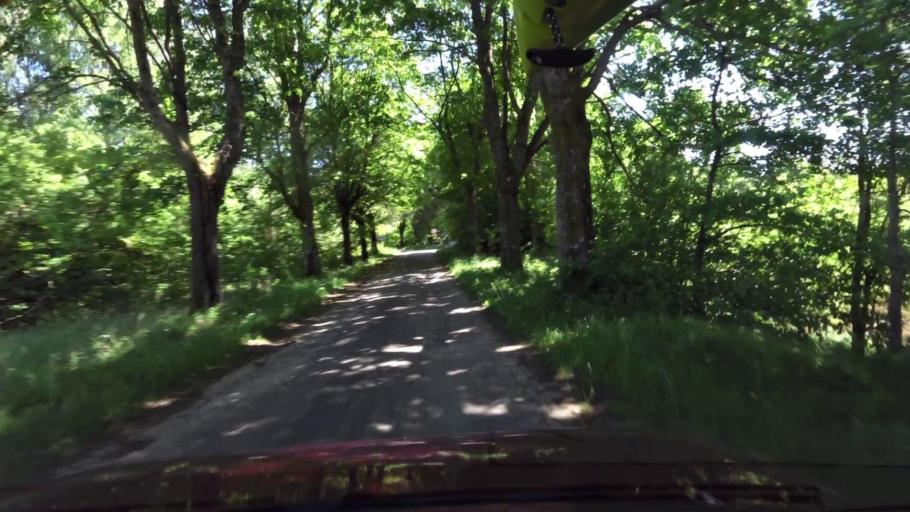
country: PL
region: West Pomeranian Voivodeship
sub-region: Powiat koszalinski
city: Polanow
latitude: 54.0368
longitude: 16.7775
